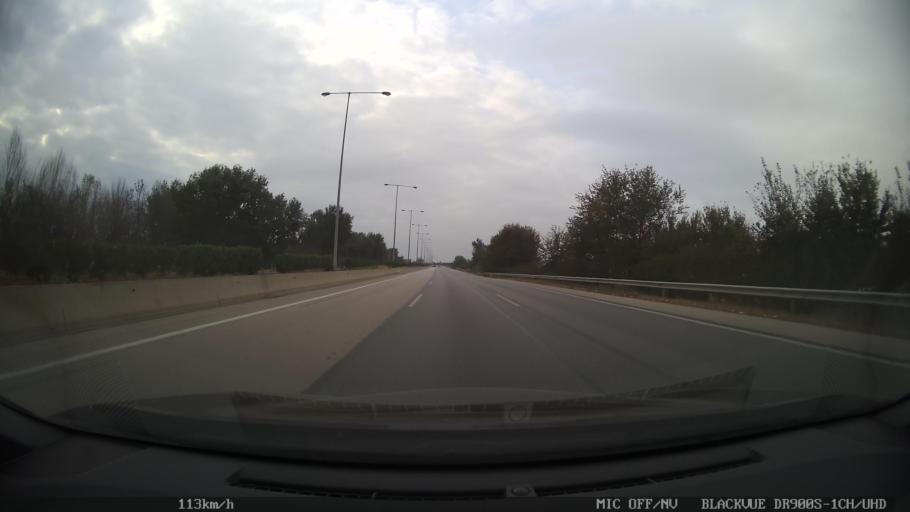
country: GR
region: Central Macedonia
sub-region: Nomos Thessalonikis
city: Nea Magnisia
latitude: 40.6837
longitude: 22.8325
